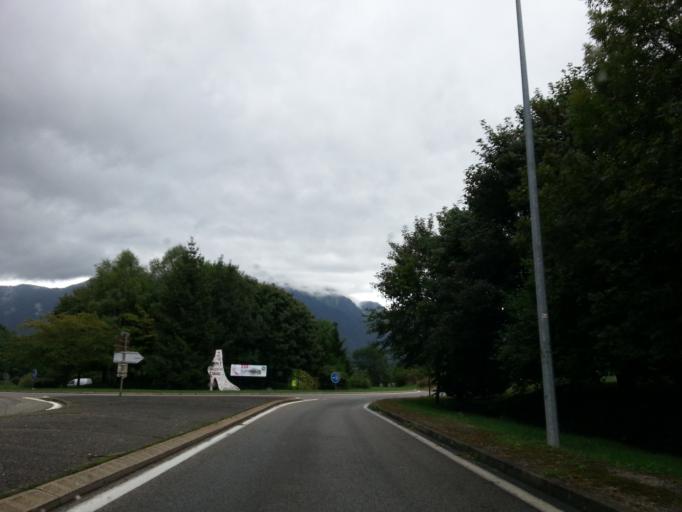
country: FR
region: Rhone-Alpes
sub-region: Departement de la Haute-Savoie
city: Faverges
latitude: 45.7568
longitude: 6.2703
